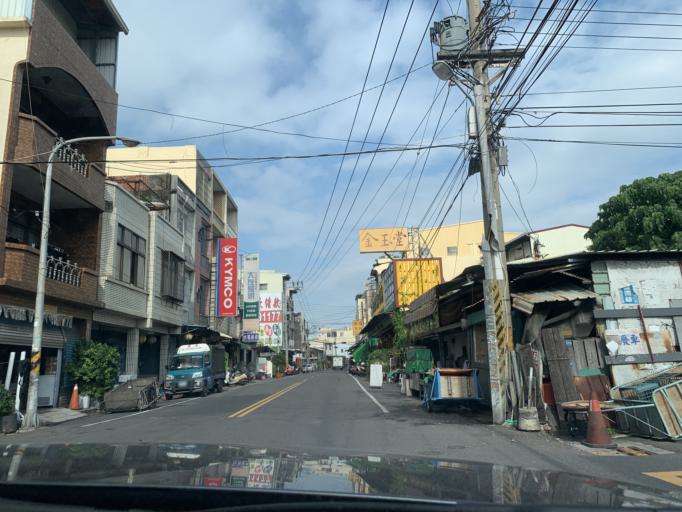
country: TW
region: Taiwan
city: Fengshan
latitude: 22.4670
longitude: 120.4471
